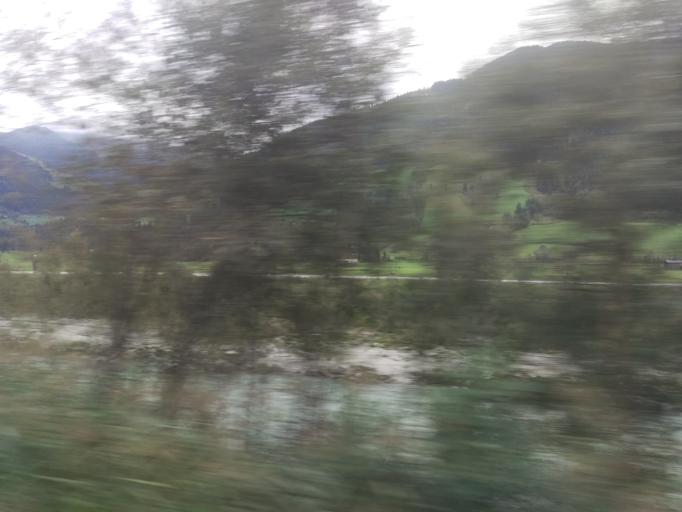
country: AT
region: Salzburg
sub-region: Politischer Bezirk Zell am See
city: Mittersill
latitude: 47.2836
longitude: 12.4596
